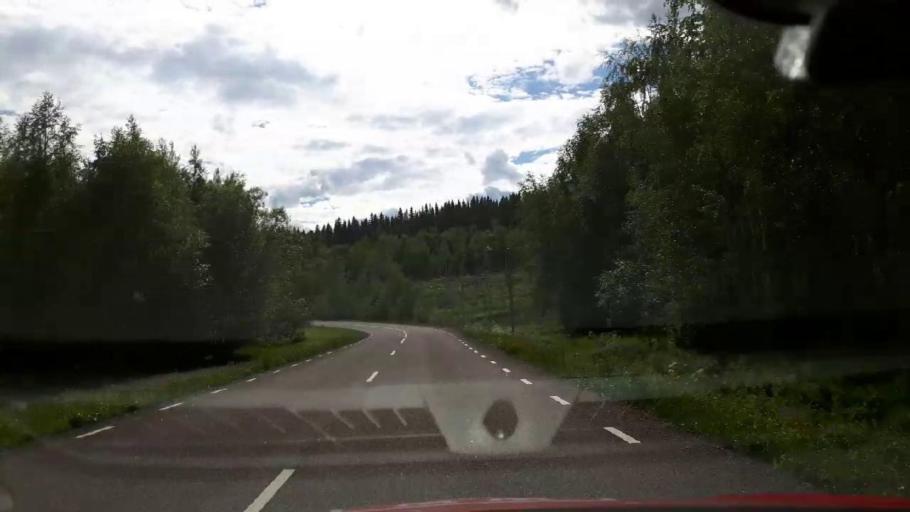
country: SE
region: Jaemtland
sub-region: Krokoms Kommun
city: Valla
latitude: 63.9342
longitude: 14.2157
